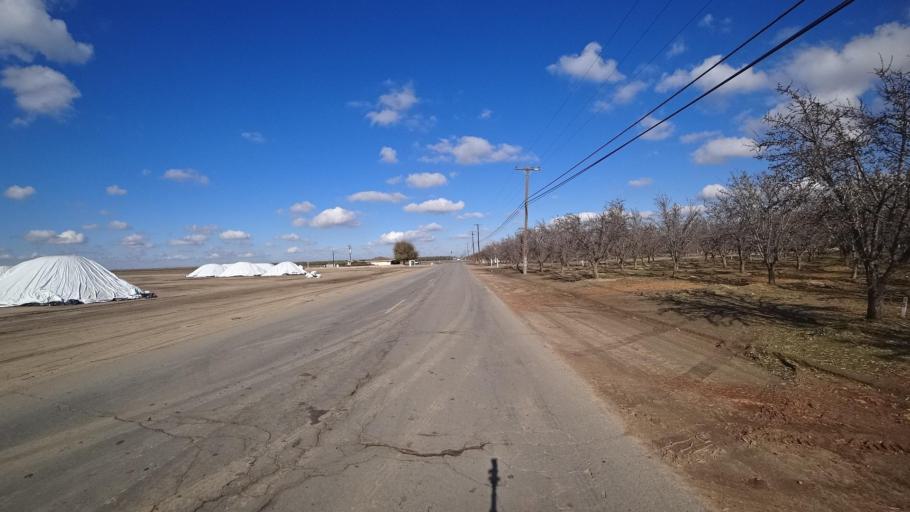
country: US
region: California
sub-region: Kern County
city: McFarland
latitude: 35.6985
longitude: -119.2408
